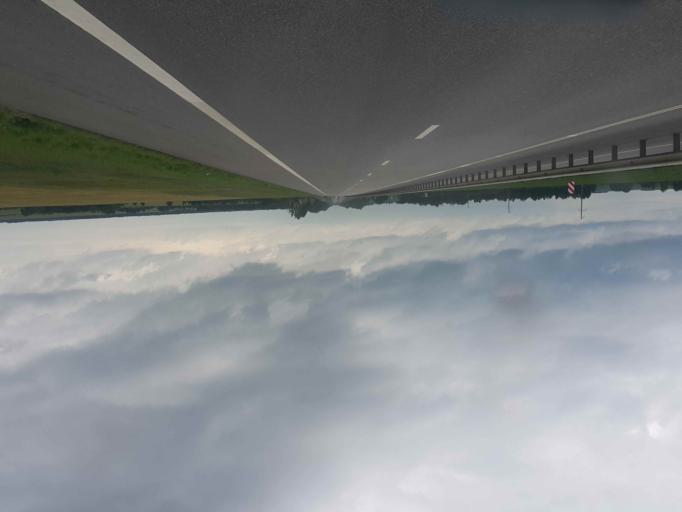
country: RU
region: Tambov
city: Selezni
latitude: 52.8181
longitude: 40.9330
